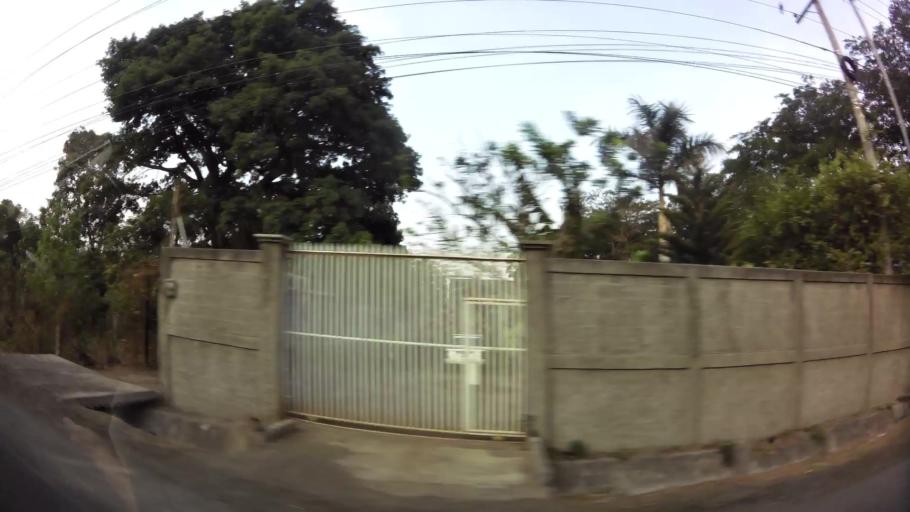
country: NI
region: Managua
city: Ciudad Sandino
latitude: 12.1509
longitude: -86.3366
